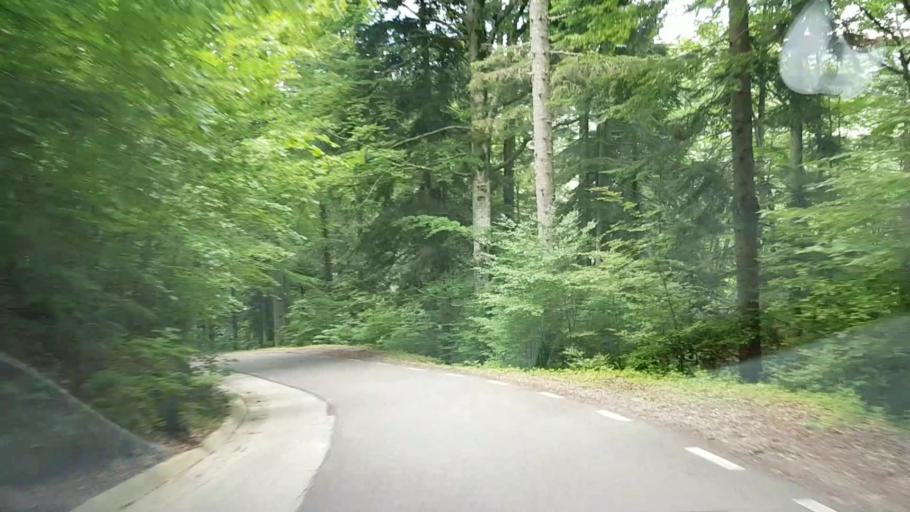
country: RO
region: Suceava
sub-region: Comuna Crucea
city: Crucea
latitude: 47.4315
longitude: 25.5730
